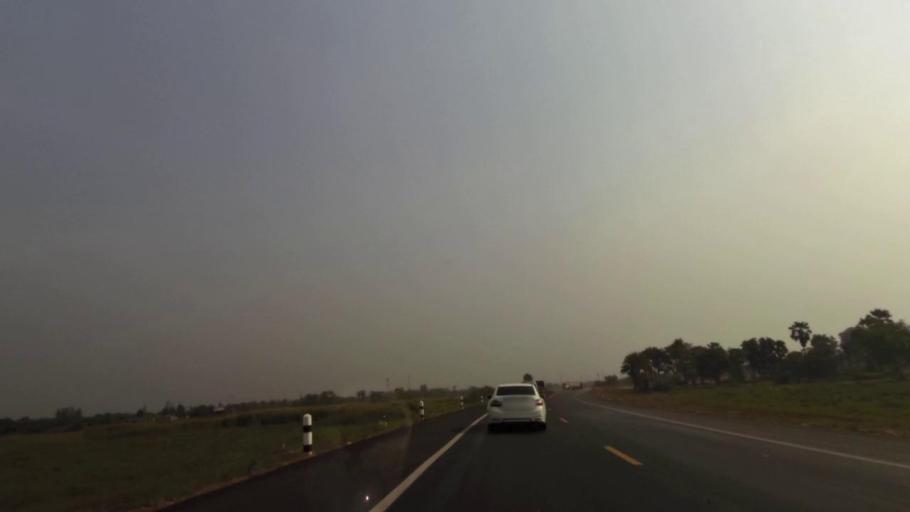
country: TH
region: Rayong
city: Klaeng
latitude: 12.7923
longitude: 101.6740
